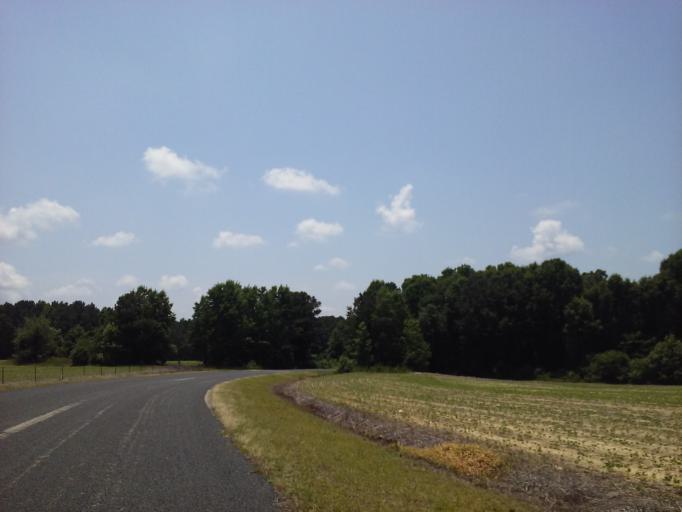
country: US
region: North Carolina
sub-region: Wake County
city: Fuquay-Varina
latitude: 35.5416
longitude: -78.8759
